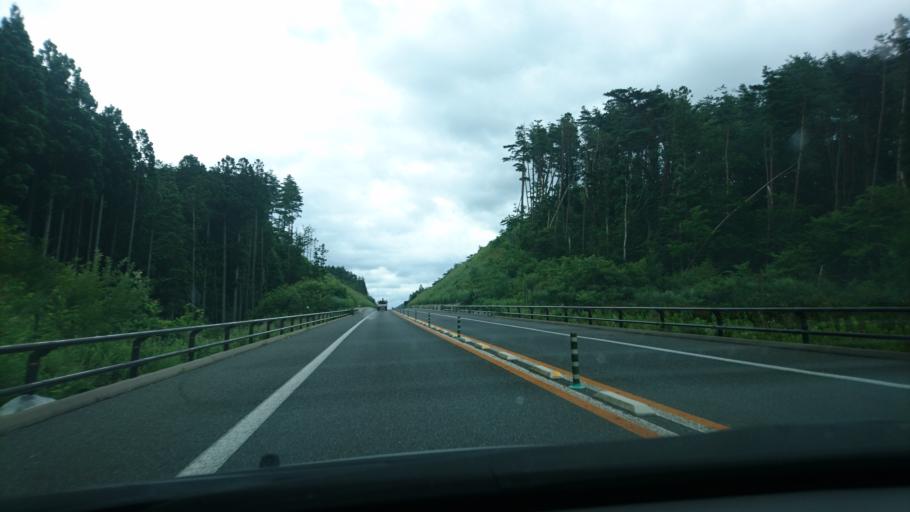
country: JP
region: Iwate
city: Ofunato
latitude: 39.0310
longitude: 141.6425
